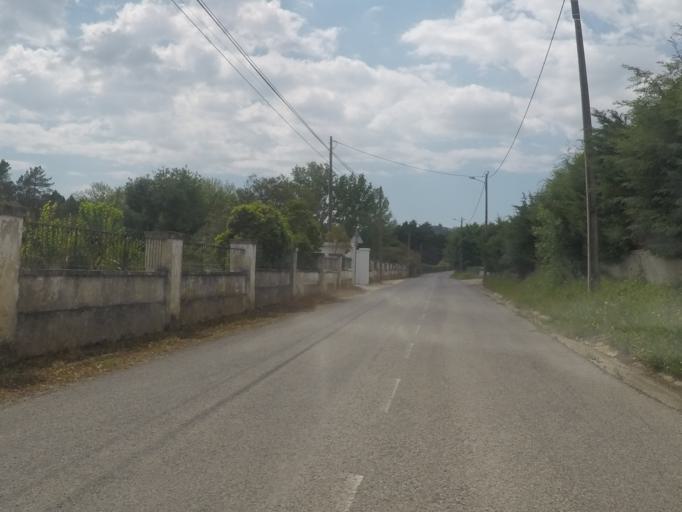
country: PT
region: Setubal
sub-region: Palmela
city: Quinta do Anjo
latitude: 38.4991
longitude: -8.9923
